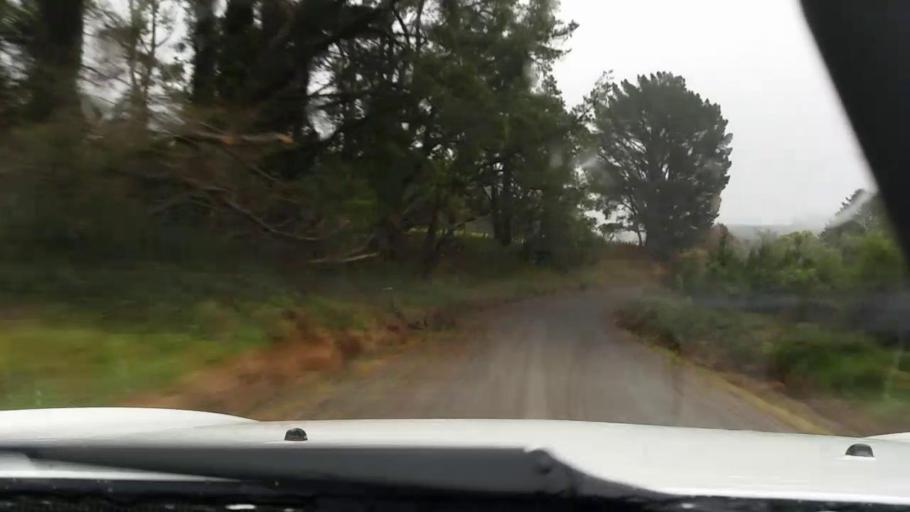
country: NZ
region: Wellington
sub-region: Masterton District
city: Masterton
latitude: -41.1822
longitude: 175.8259
